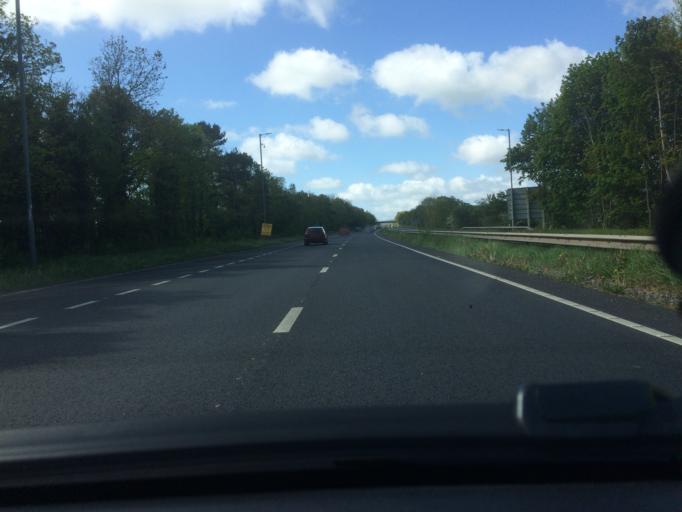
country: GB
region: Wales
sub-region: Wrexham
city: Wrexham
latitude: 53.0694
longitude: -2.9925
